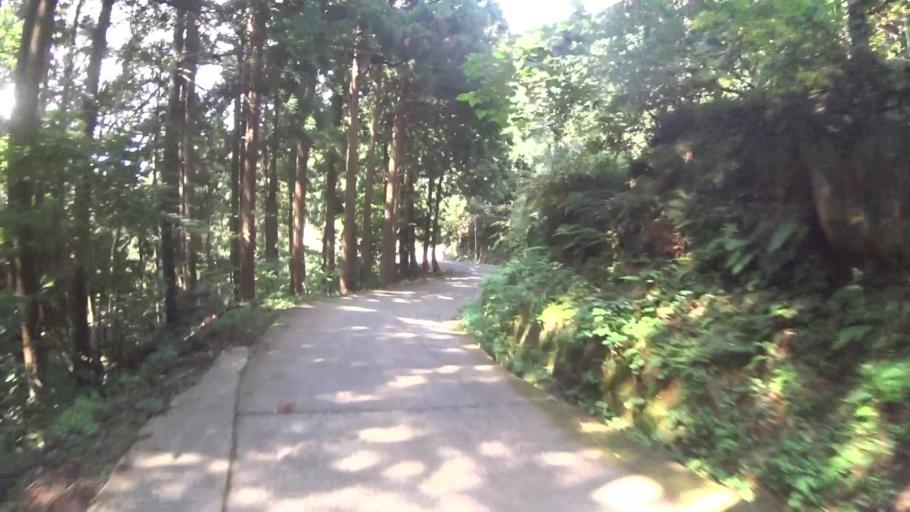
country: JP
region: Kyoto
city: Miyazu
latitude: 35.7398
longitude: 135.1884
